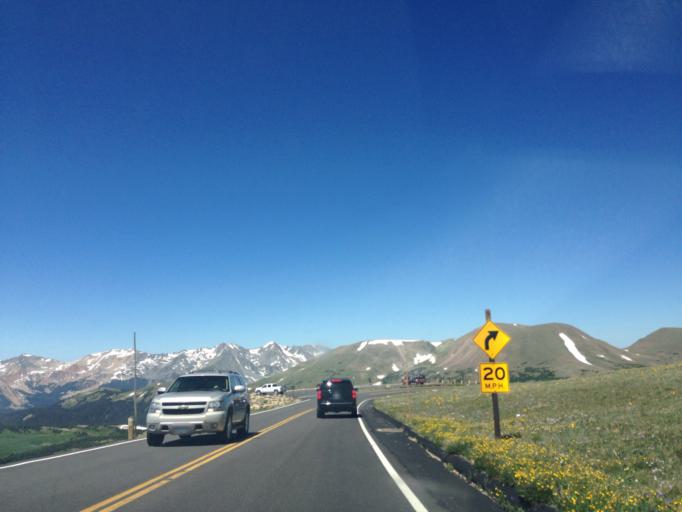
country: US
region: Colorado
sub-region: Larimer County
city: Estes Park
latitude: 40.4325
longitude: -105.7668
